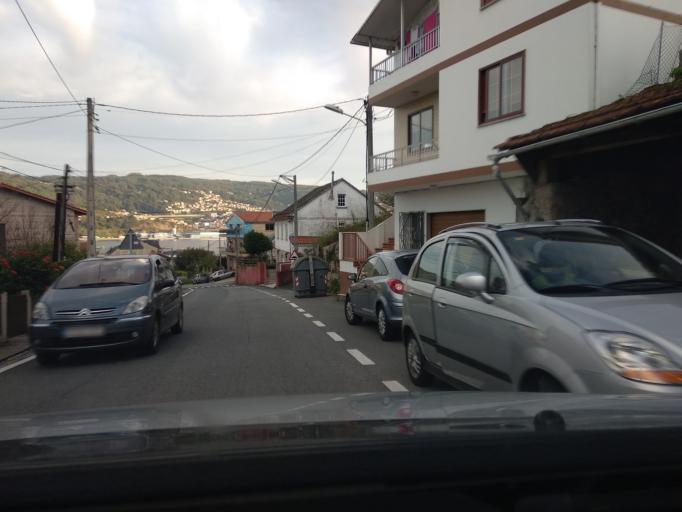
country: ES
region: Galicia
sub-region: Provincia de Pontevedra
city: Moana
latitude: 42.2874
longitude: -8.6854
